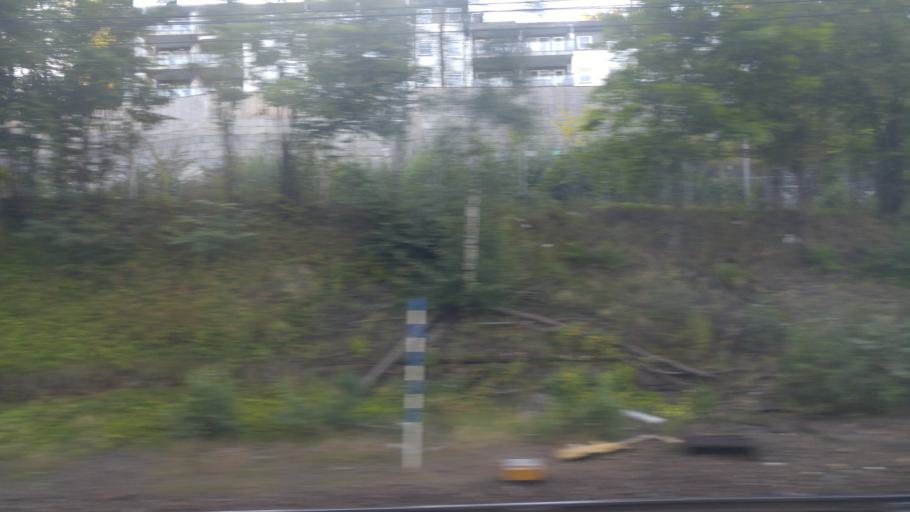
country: NO
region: Oslo
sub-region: Oslo
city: Oslo
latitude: 59.9108
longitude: 10.8247
